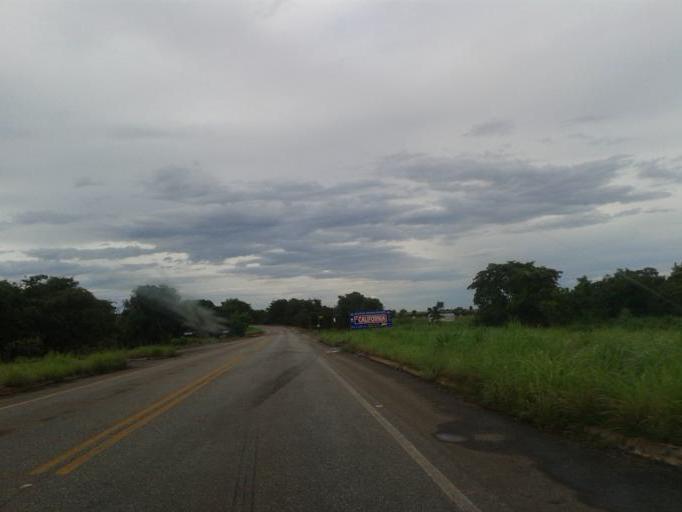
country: BR
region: Goias
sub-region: Mozarlandia
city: Mozarlandia
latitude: -14.8057
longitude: -50.5333
